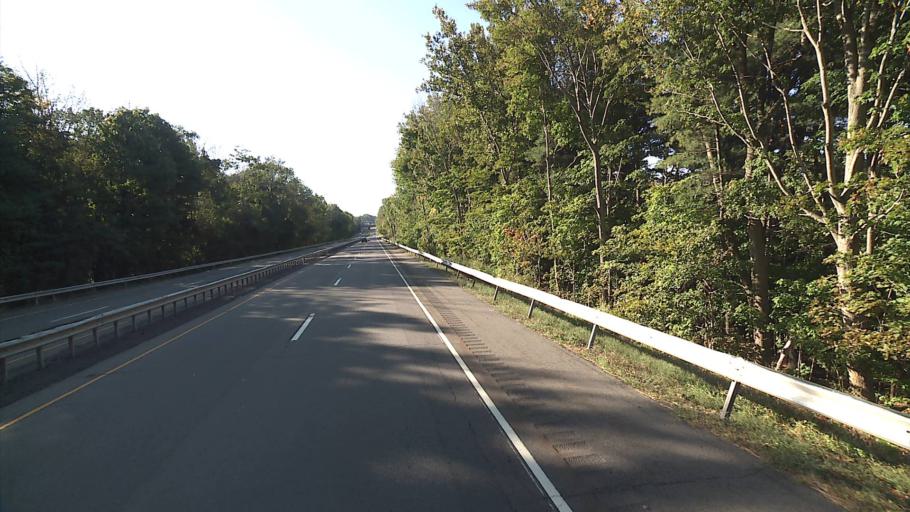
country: US
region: Connecticut
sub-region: New Haven County
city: Meriden
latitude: 41.5484
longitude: -72.7732
